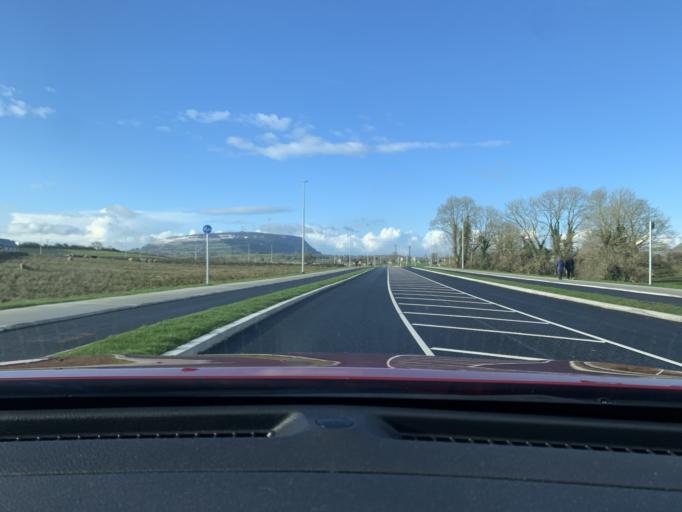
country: IE
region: Connaught
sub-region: Sligo
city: Sligo
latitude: 54.2597
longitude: -8.4947
